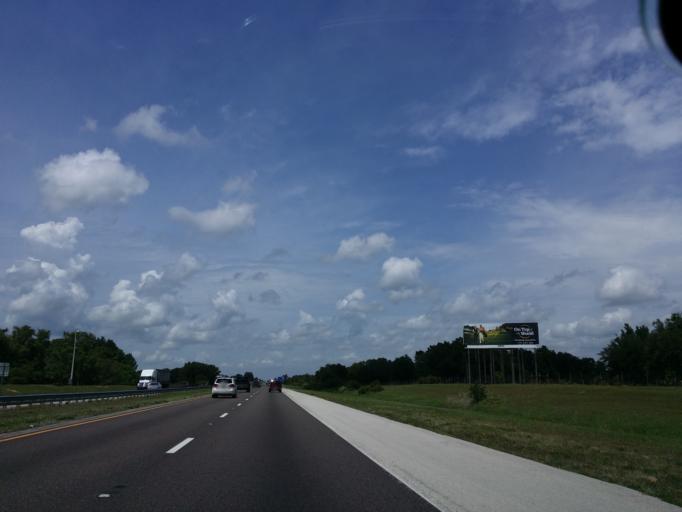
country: US
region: Florida
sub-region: Lake County
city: Hawthorne
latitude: 28.6956
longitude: -81.8755
